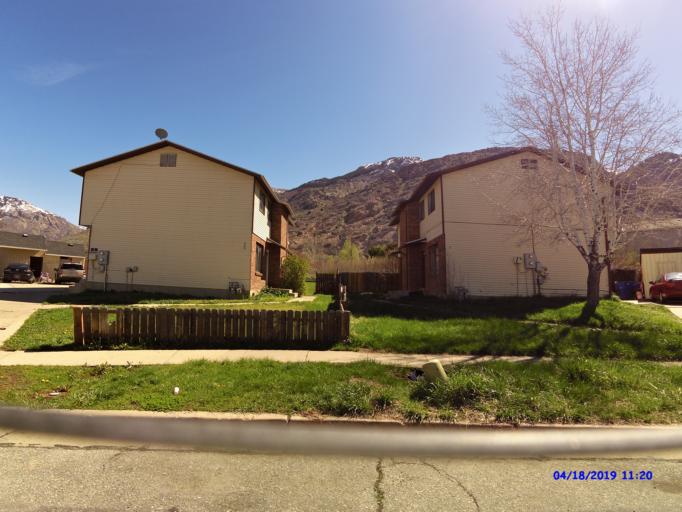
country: US
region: Utah
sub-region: Weber County
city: North Ogden
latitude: 41.2795
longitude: -111.9542
